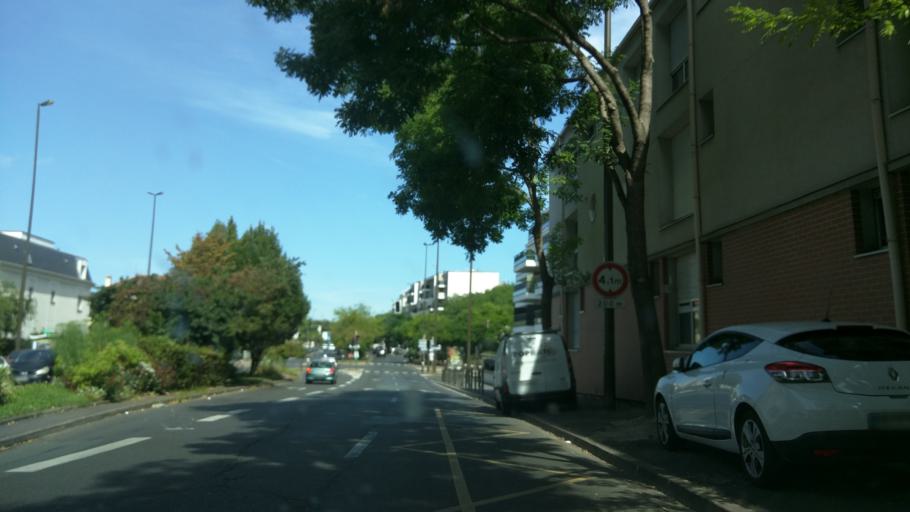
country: FR
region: Ile-de-France
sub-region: Departement des Yvelines
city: Sartrouville
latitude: 48.9405
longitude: 2.2070
